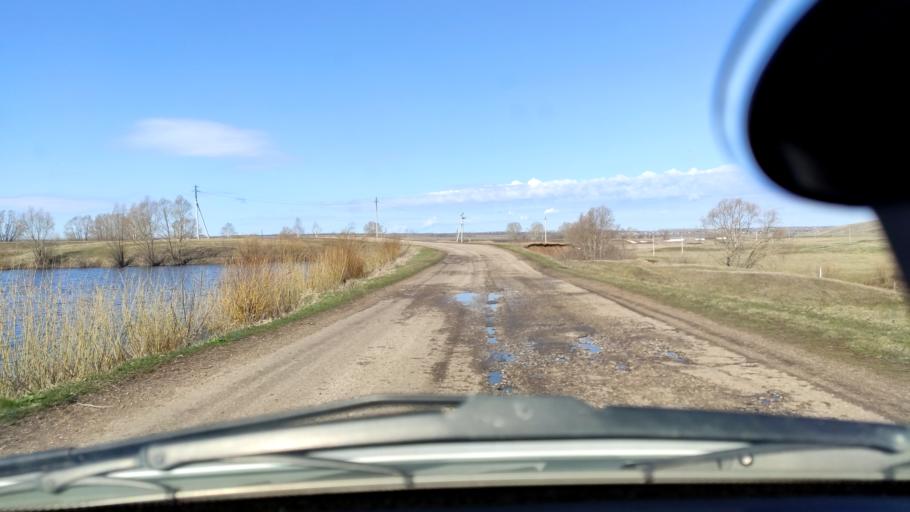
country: RU
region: Bashkortostan
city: Tolbazy
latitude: 54.1728
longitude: 55.9511
